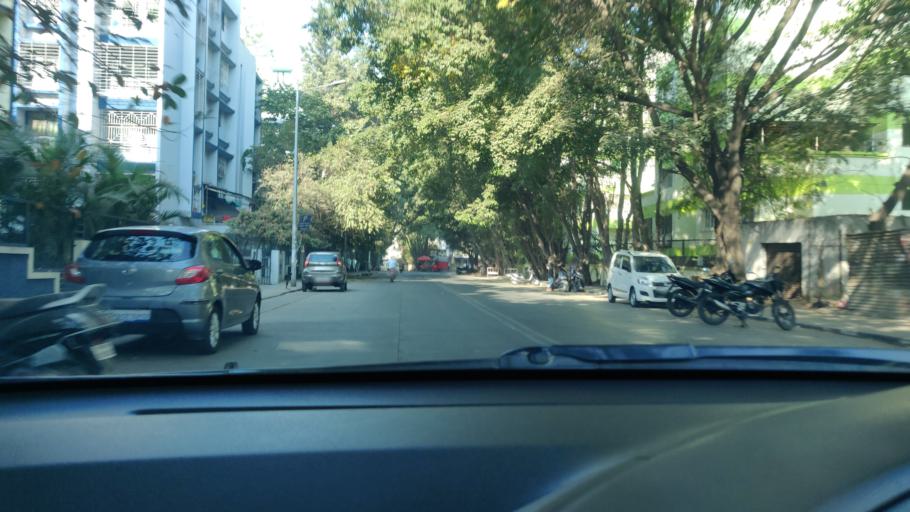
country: IN
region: Maharashtra
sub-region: Pune Division
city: Khadki
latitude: 18.5537
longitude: 73.8060
